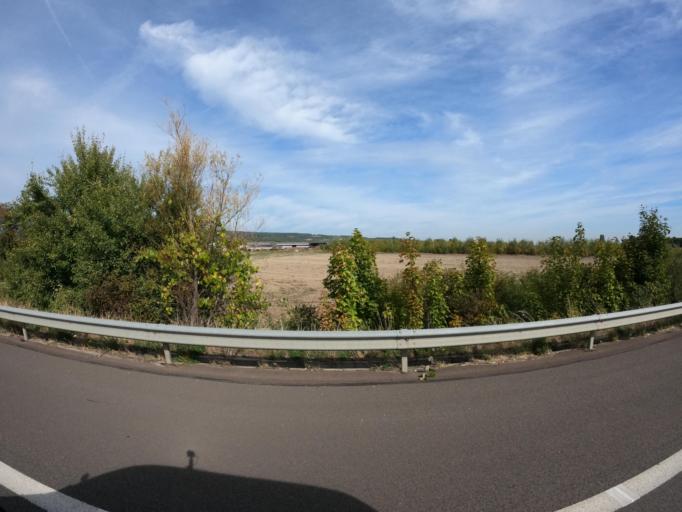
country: FR
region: Bourgogne
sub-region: Departement de Saone-et-Loire
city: Givry
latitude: 46.7596
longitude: 4.7381
